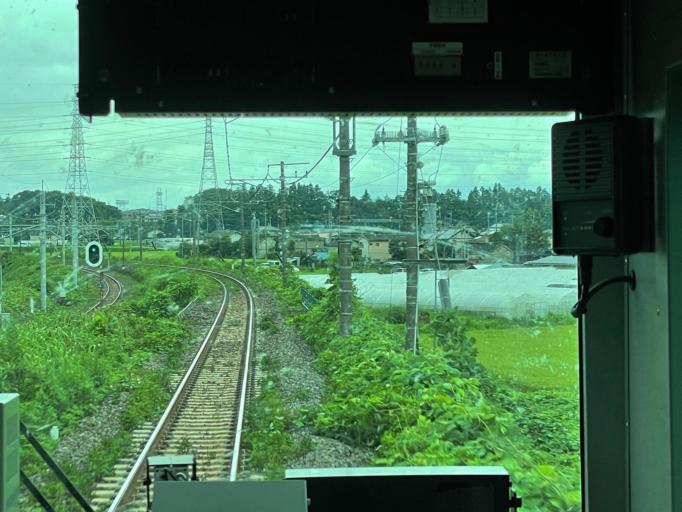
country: JP
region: Tochigi
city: Ujiie
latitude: 36.6108
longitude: 139.9666
